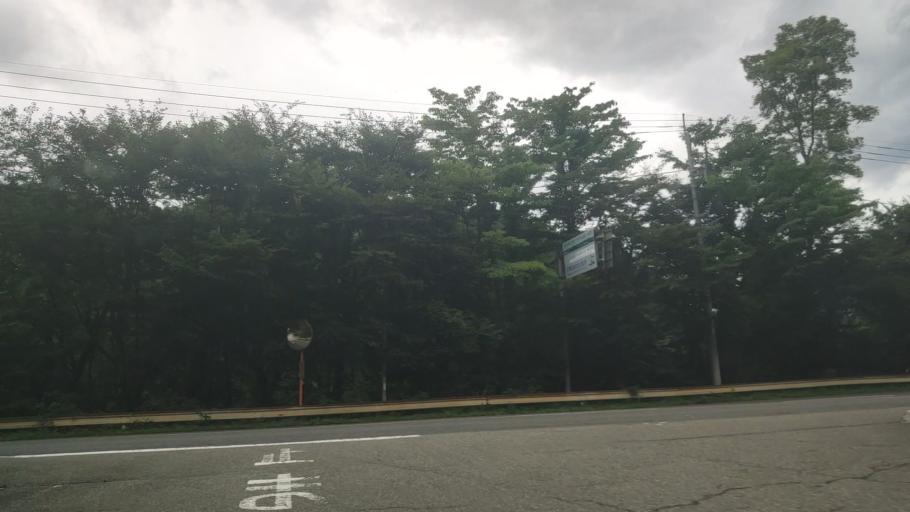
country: JP
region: Tochigi
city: Nikko
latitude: 36.6399
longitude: 139.4493
